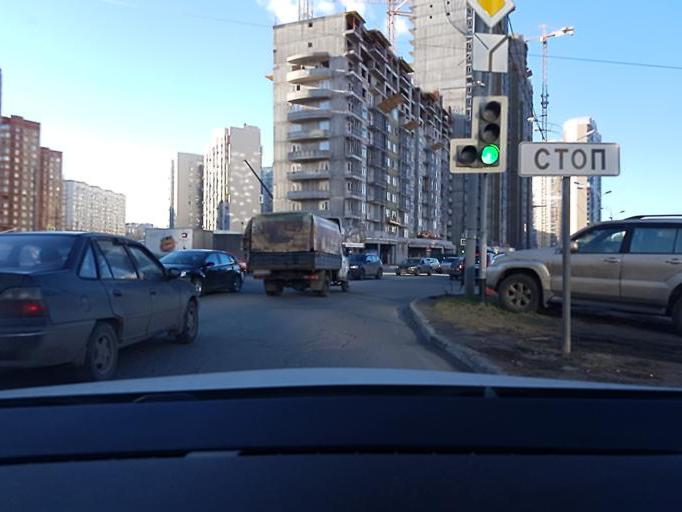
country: RU
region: Moskovskaya
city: Pavshino
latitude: 55.8243
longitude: 37.3746
